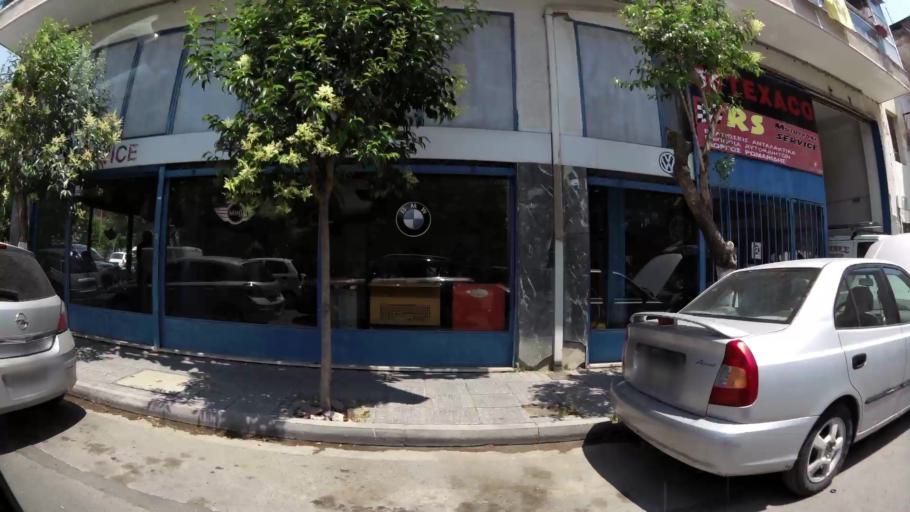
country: GR
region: Central Macedonia
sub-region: Nomos Thessalonikis
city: Ampelokipoi
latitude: 40.6558
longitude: 22.9155
